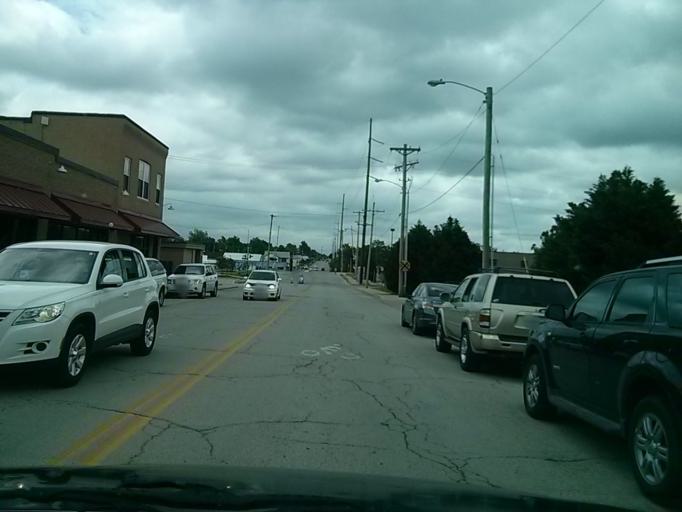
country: US
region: Oklahoma
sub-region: Tulsa County
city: Tulsa
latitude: 36.1567
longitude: -95.9797
